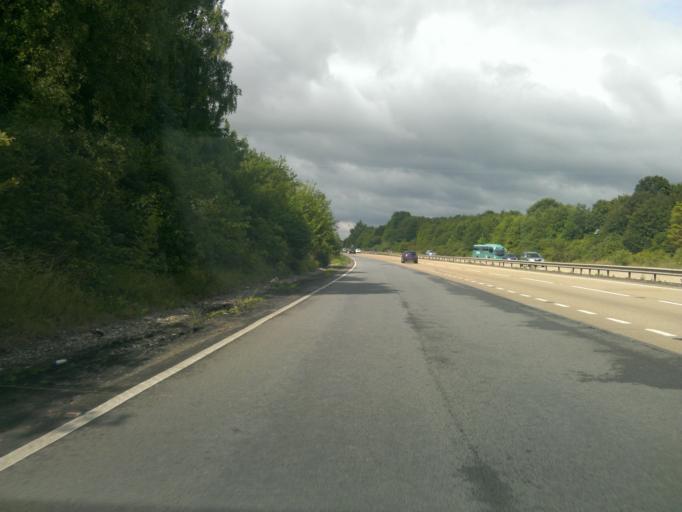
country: GB
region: England
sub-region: Essex
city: Great Bentley
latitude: 51.8854
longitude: 1.0410
